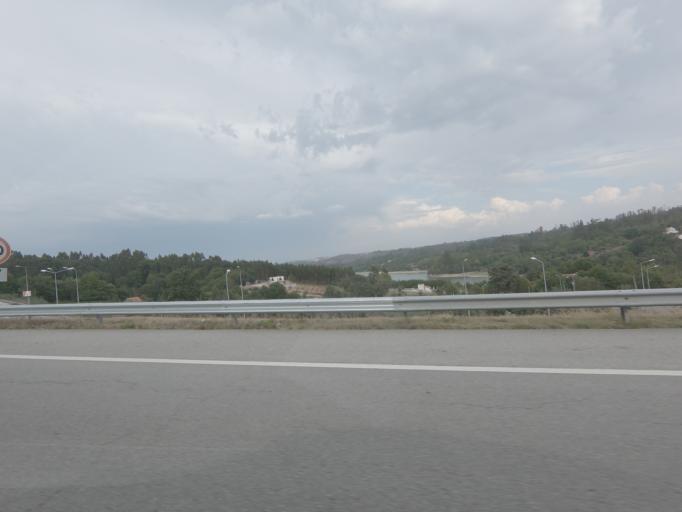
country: PT
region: Viseu
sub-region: Santa Comba Dao
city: Santa Comba Dao
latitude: 40.3999
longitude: -8.1261
